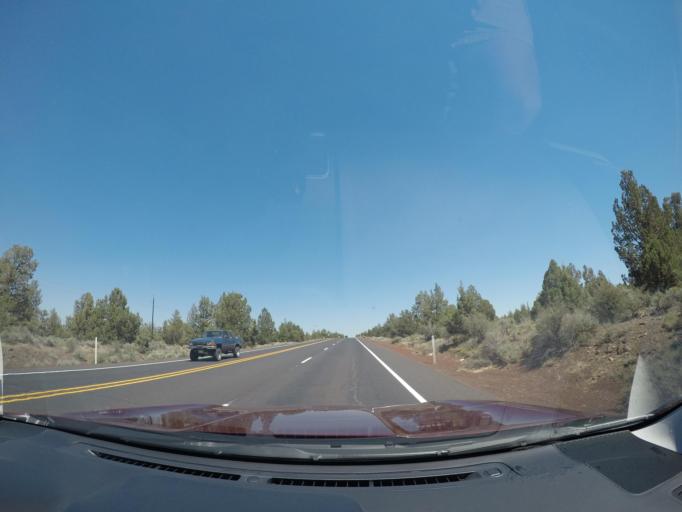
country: US
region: Oregon
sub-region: Deschutes County
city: Sisters
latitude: 44.2949
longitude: -121.3888
